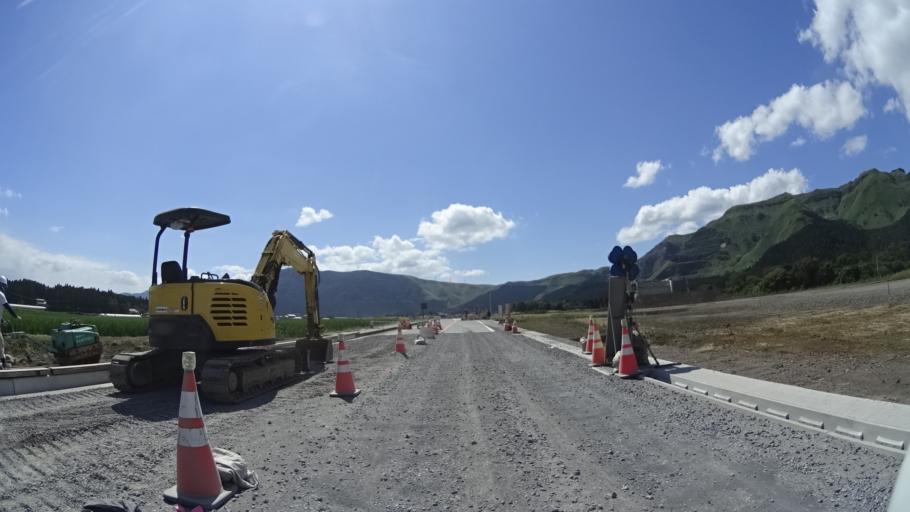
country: JP
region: Kumamoto
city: Aso
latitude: 32.9247
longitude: 130.9956
